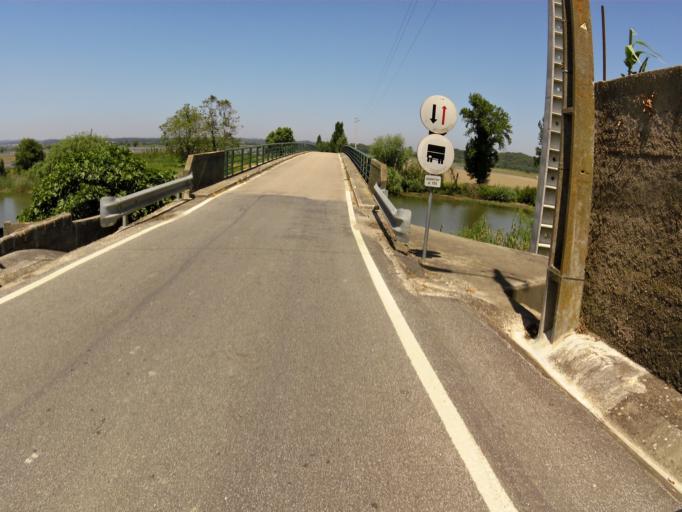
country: PT
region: Coimbra
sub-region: Montemor-O-Velho
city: Montemor-o-Velho
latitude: 40.1593
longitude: -8.7140
